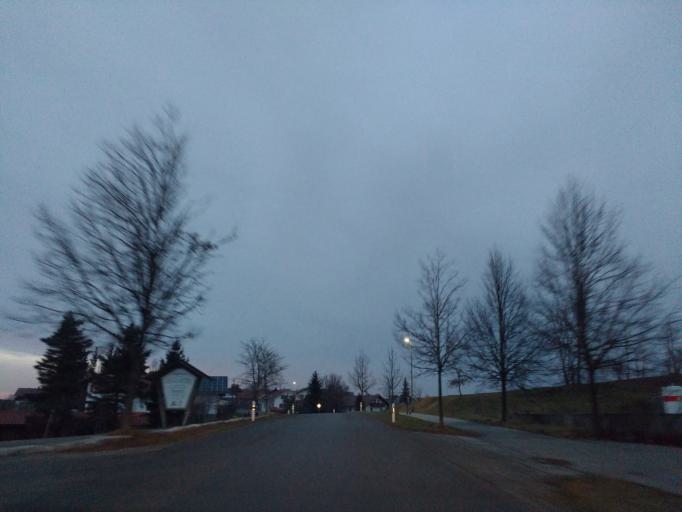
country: DE
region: Bavaria
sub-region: Upper Bavaria
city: Bernbeuren
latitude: 47.7705
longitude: 10.7502
